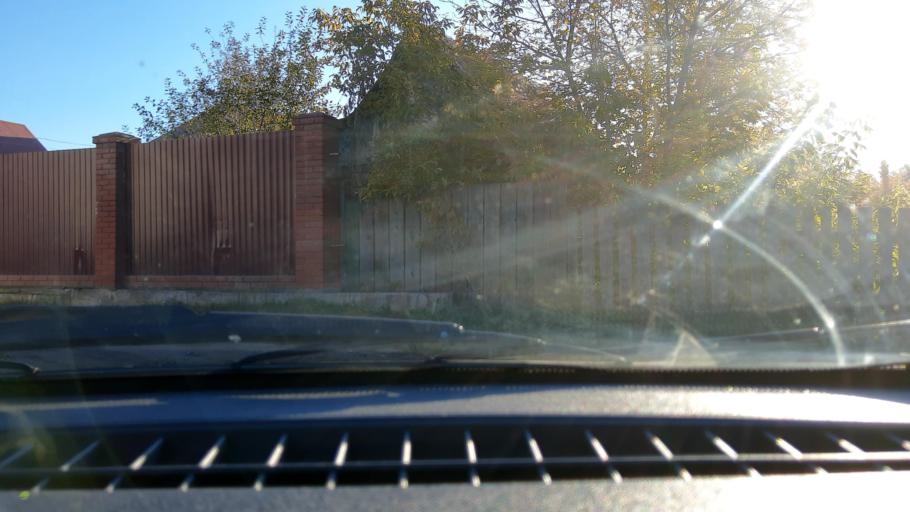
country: RU
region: Bashkortostan
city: Ufa
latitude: 54.6924
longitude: 55.9498
